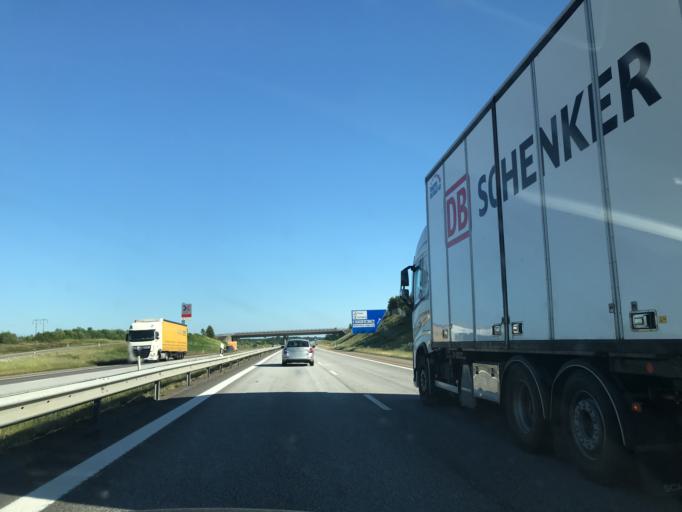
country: SE
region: Halland
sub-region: Varbergs Kommun
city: Tvaaker
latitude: 57.0607
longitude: 12.3577
